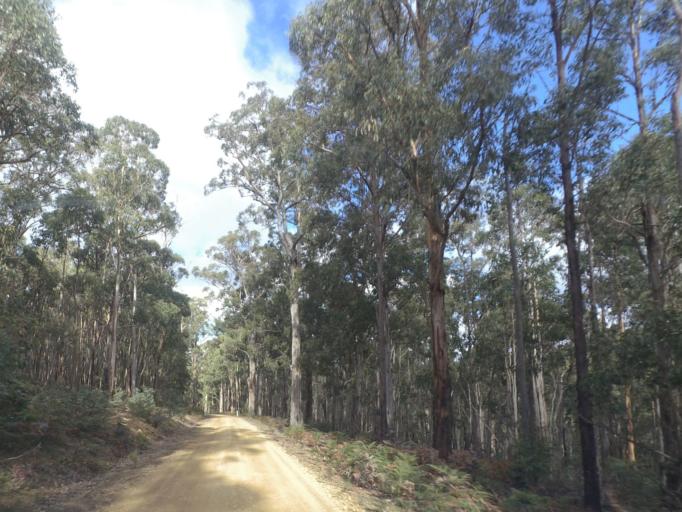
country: AU
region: Victoria
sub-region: Moorabool
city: Bacchus Marsh
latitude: -37.4621
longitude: 144.4401
